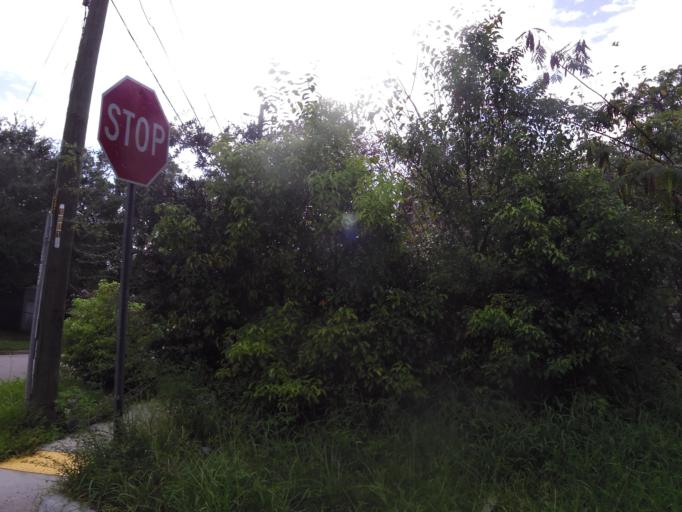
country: US
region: Florida
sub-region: Duval County
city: Jacksonville
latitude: 30.3588
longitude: -81.6830
